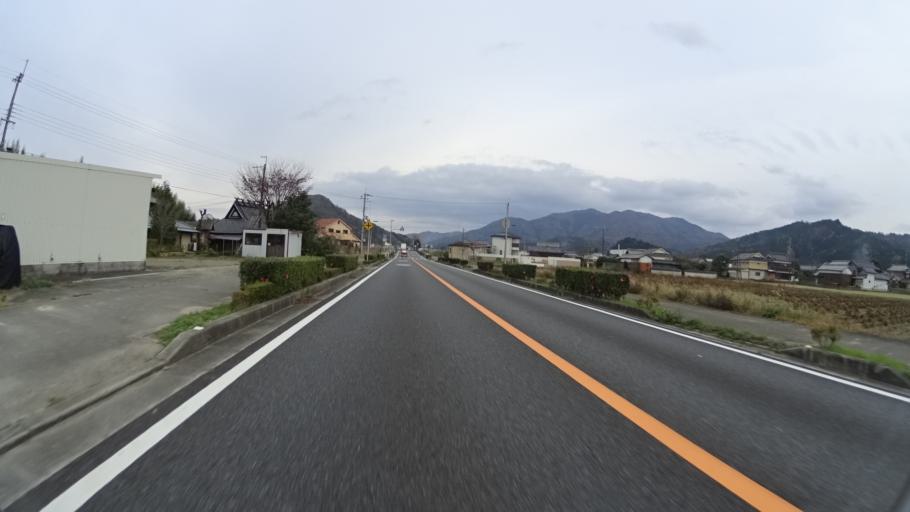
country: JP
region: Hyogo
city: Sasayama
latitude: 35.0704
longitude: 135.2716
